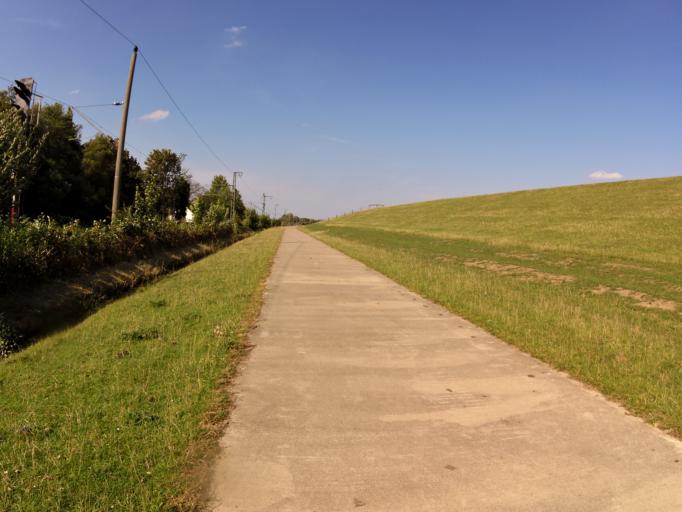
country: DE
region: Lower Saxony
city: Nordenham
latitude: 53.4466
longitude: 8.4760
